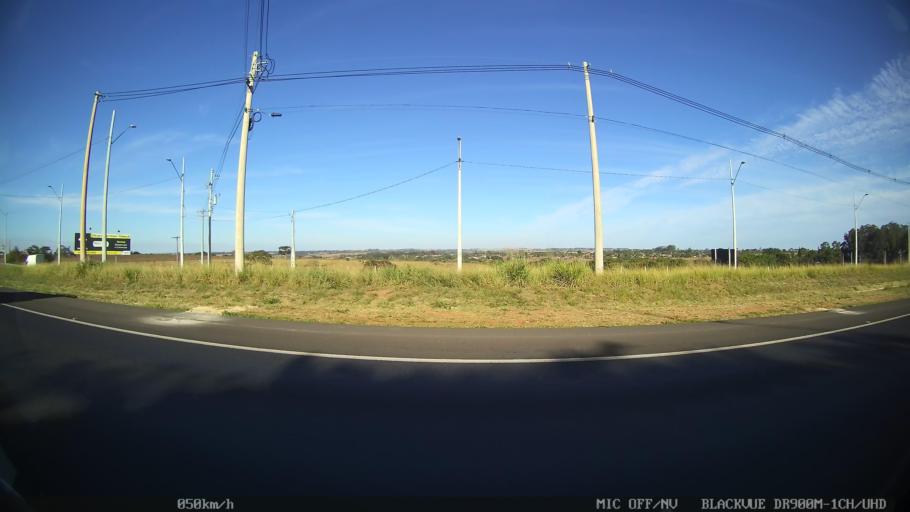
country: BR
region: Sao Paulo
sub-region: Sao Jose Do Rio Preto
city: Sao Jose do Rio Preto
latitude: -20.8548
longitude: -49.4041
